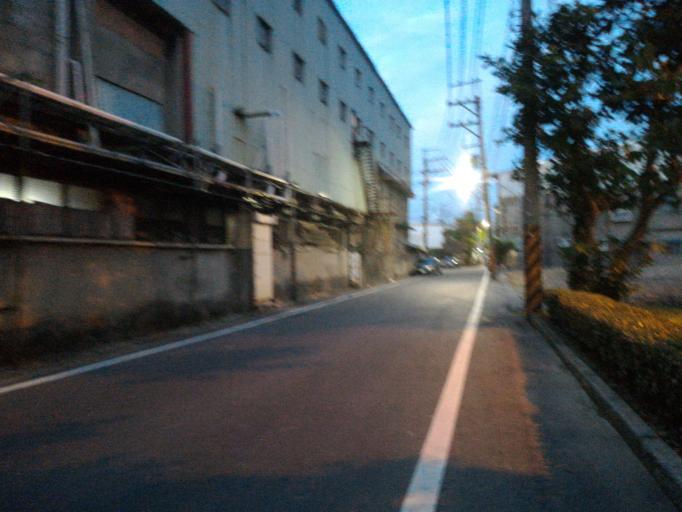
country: TW
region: Taipei
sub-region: Taipei
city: Banqiao
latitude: 24.9616
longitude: 121.4004
